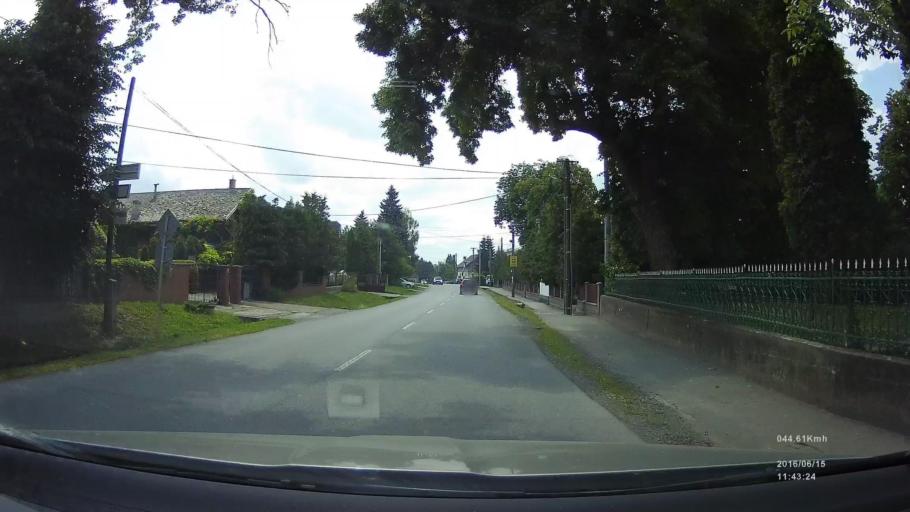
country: SK
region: Kosicky
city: Kosice
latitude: 48.7521
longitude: 21.3439
